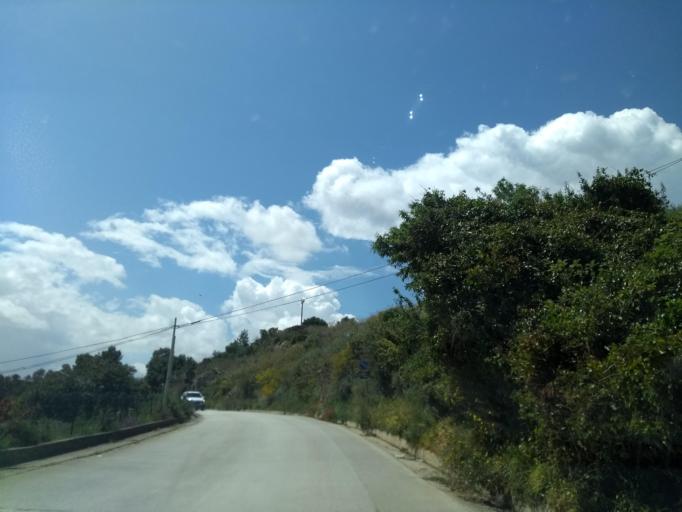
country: IT
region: Sicily
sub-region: Trapani
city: Castellammare del Golfo
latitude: 38.0578
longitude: 12.8382
